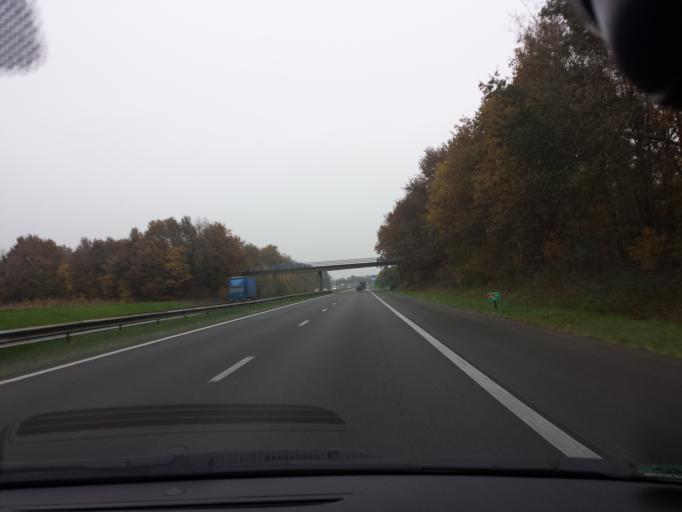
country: NL
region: Gelderland
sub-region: Gemeente Wijchen
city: Wijchen
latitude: 51.8215
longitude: 5.7202
